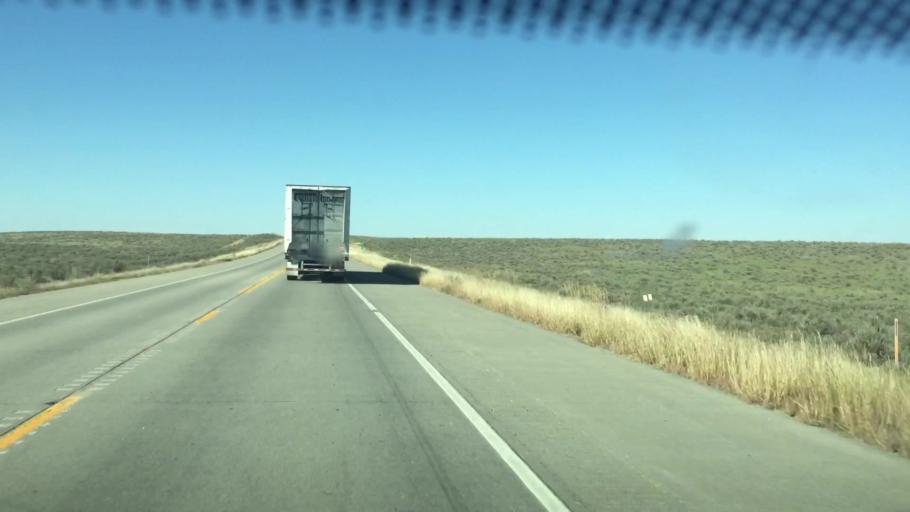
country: US
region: Colorado
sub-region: Kiowa County
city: Eads
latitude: 38.5737
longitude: -102.7846
